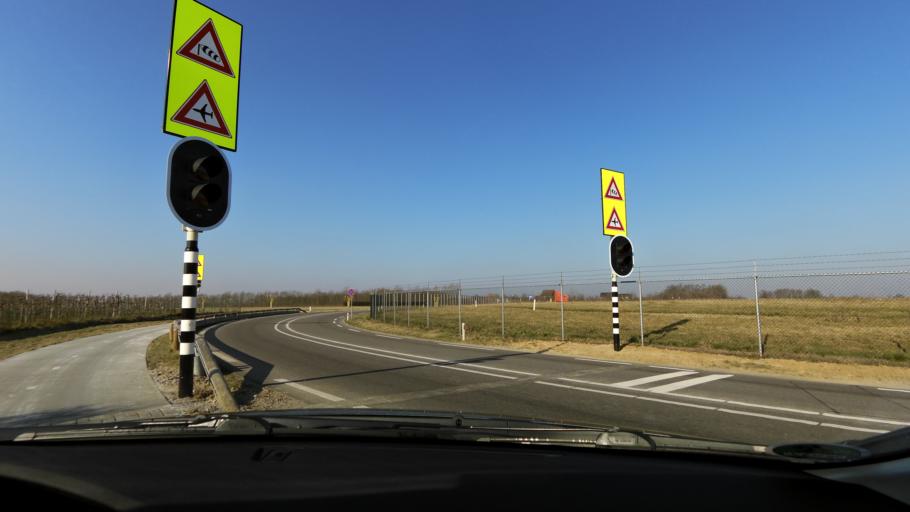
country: NL
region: Limburg
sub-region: Gemeente Meerssen
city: Meerssen
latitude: 50.8985
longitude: 5.7589
